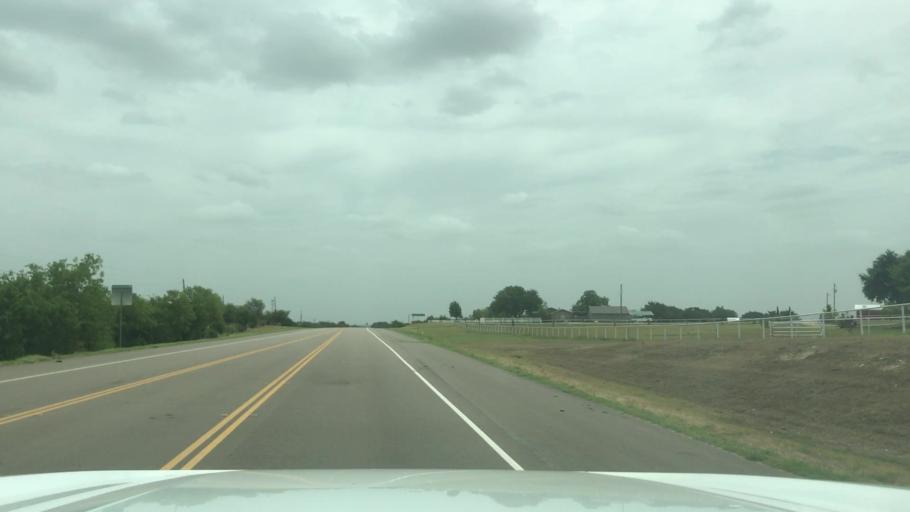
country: US
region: Texas
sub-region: McLennan County
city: Woodway
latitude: 31.5887
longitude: -97.3252
